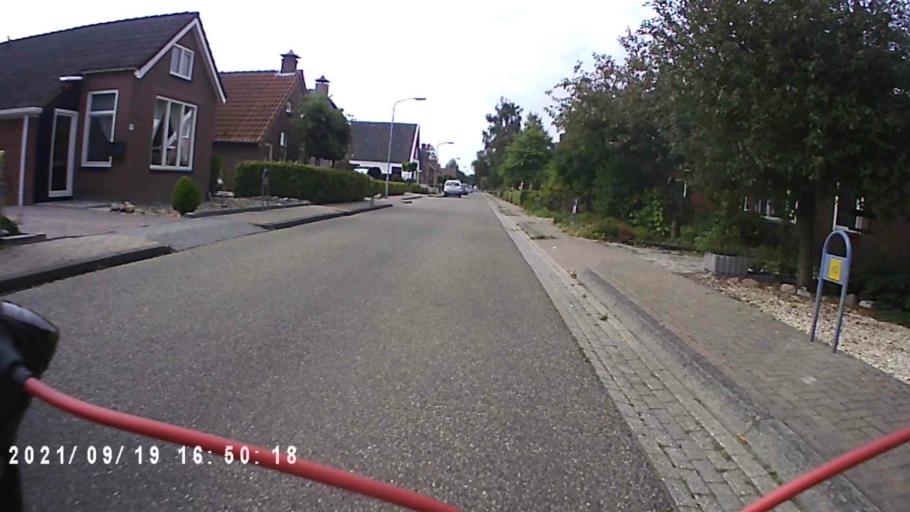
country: NL
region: Groningen
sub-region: Gemeente  Oldambt
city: Winschoten
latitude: 53.1778
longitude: 7.0891
